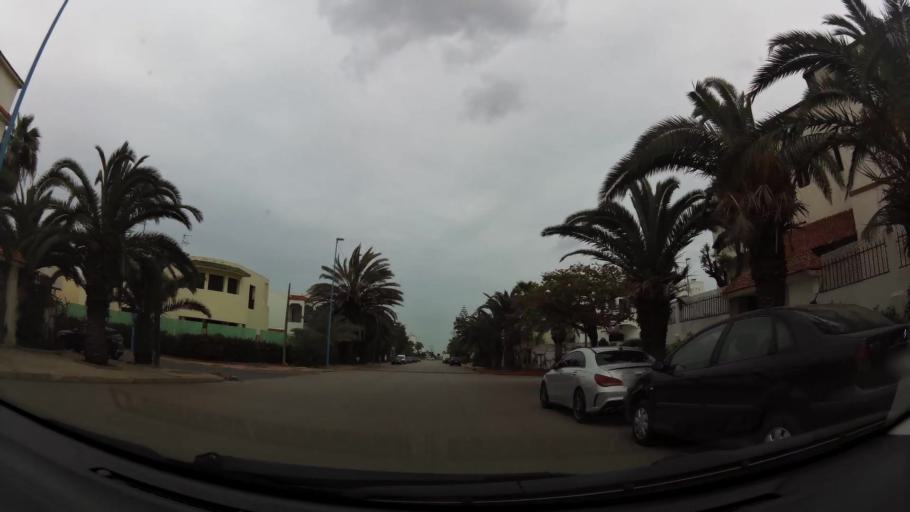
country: MA
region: Grand Casablanca
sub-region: Casablanca
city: Casablanca
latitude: 33.5989
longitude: -7.6527
